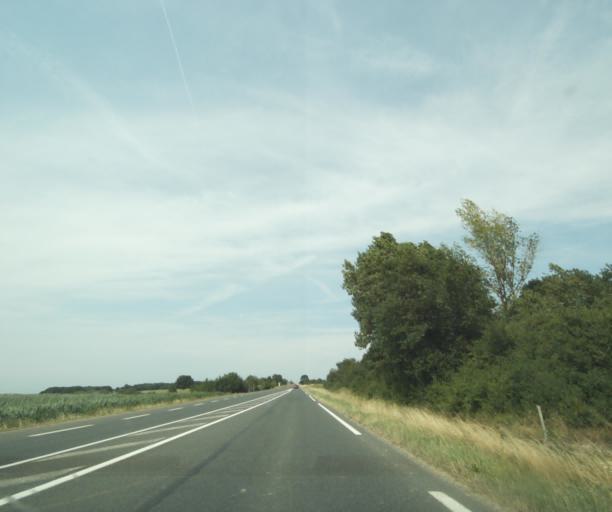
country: FR
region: Centre
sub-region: Departement d'Indre-et-Loire
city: Sorigny
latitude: 47.1851
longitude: 0.6620
